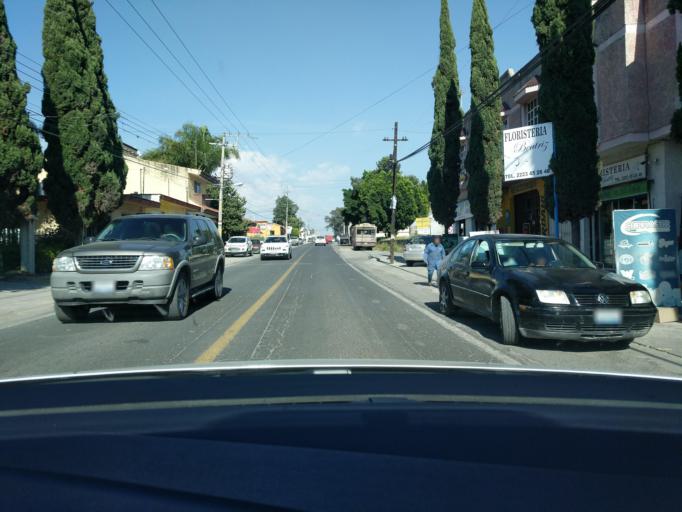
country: MX
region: Puebla
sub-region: San Gregorio Atzompa
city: Chipilo de Francisco Javier Mina
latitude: 19.0075
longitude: -98.3278
